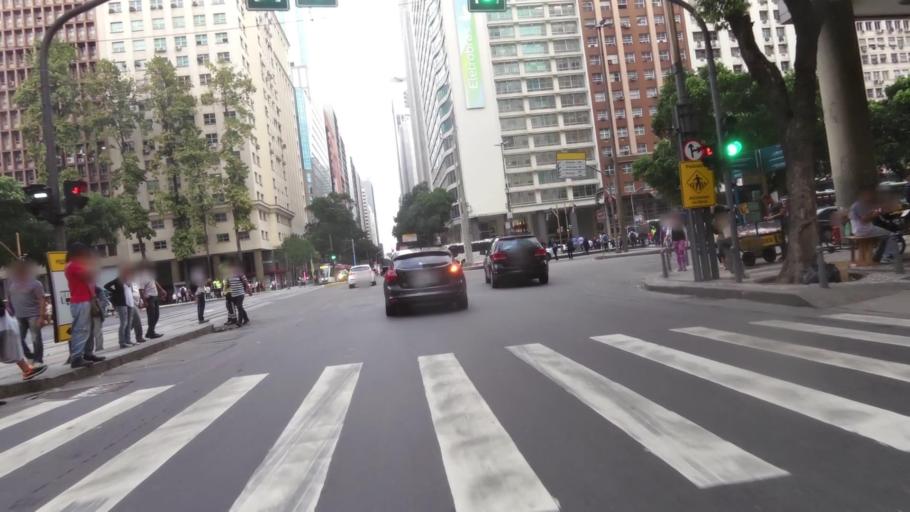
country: BR
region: Rio de Janeiro
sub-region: Rio De Janeiro
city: Rio de Janeiro
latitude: -22.9008
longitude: -43.1793
